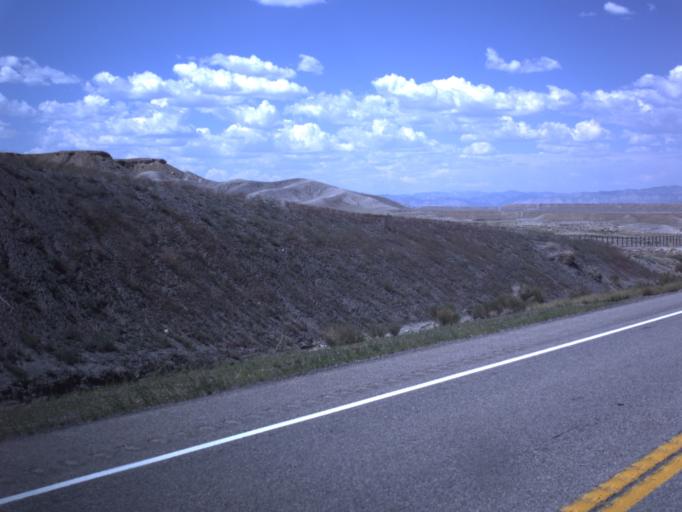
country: US
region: Utah
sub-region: Emery County
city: Huntington
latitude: 39.4174
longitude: -110.8742
